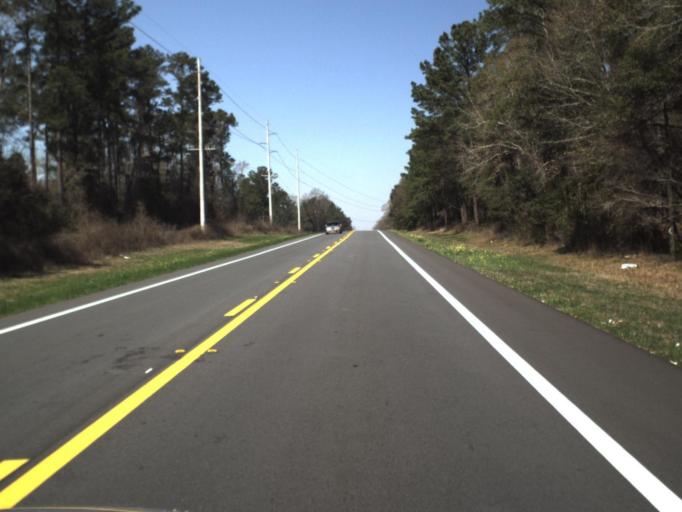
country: US
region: Florida
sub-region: Jackson County
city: Sneads
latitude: 30.8170
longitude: -85.0446
